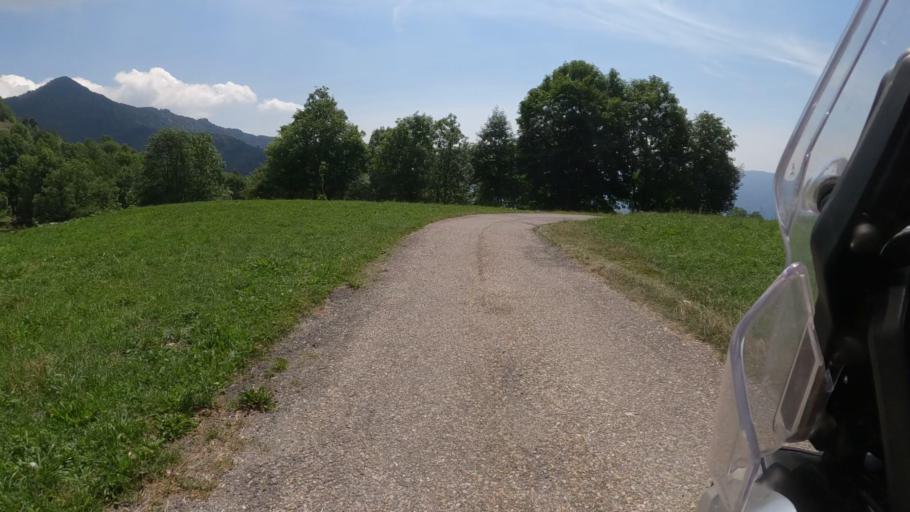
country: IT
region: Piedmont
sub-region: Provincia di Torino
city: Sant'Antonino di Susa
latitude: 45.1491
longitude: 7.2773
